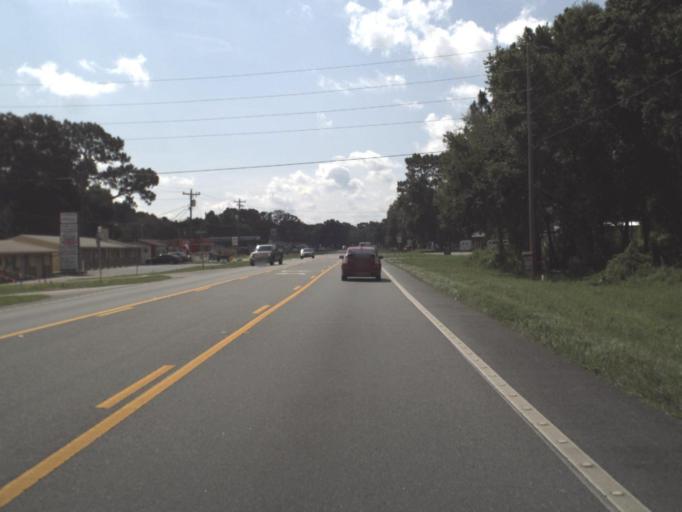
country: US
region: Florida
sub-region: Citrus County
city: Inverness Highlands North
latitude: 28.8625
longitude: -82.3530
